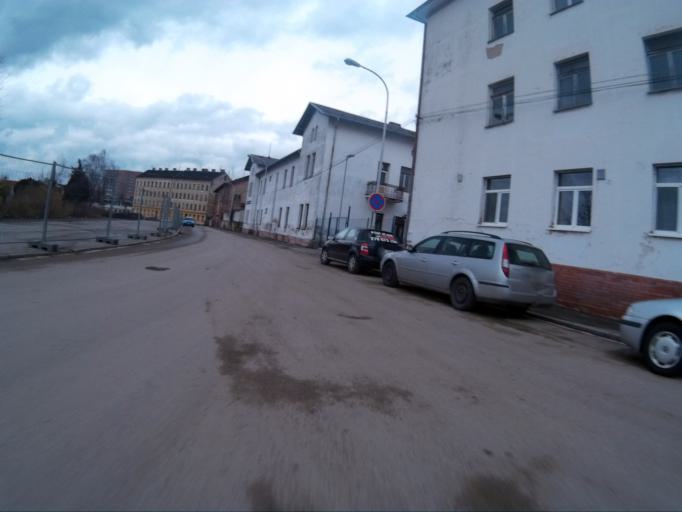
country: CZ
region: South Moravian
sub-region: Mesto Brno
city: Brno
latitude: 49.1836
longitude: 16.6158
